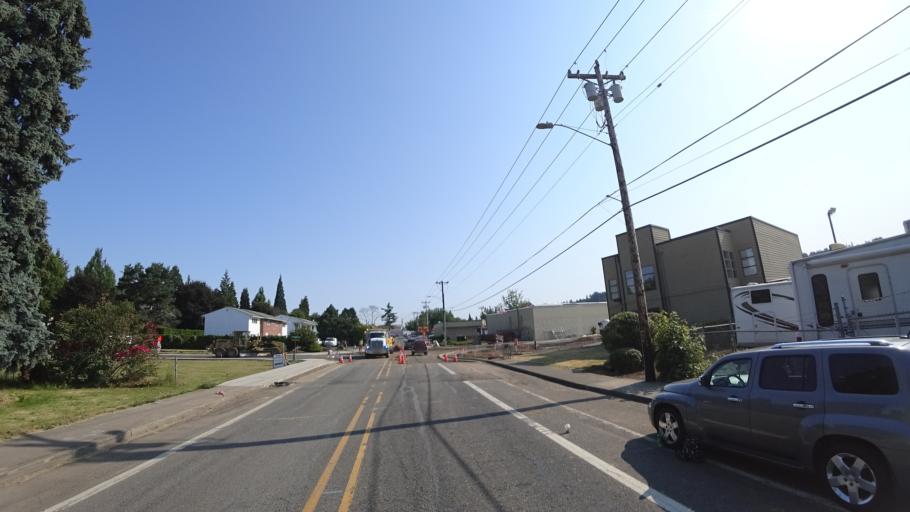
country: US
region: Oregon
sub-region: Clackamas County
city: Oatfield
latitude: 45.4442
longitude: -122.5806
